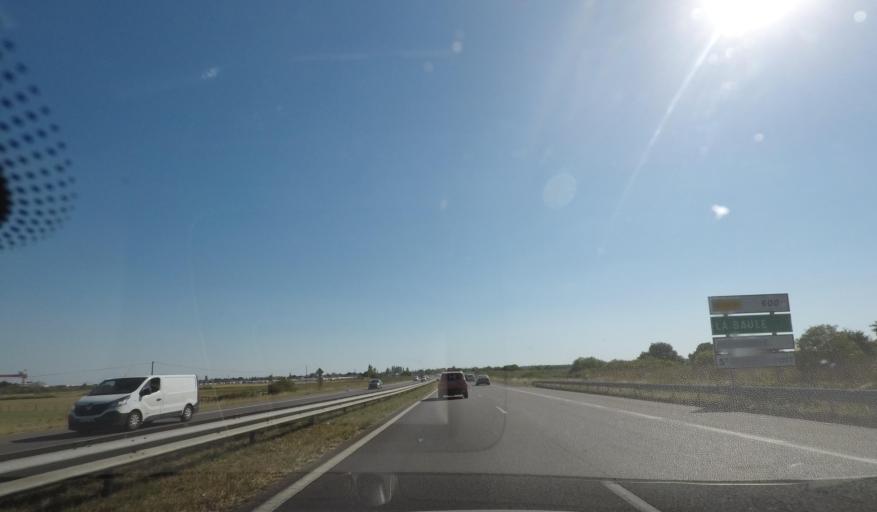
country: FR
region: Pays de la Loire
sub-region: Departement de la Loire-Atlantique
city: Trignac
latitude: 47.3148
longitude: -2.1982
